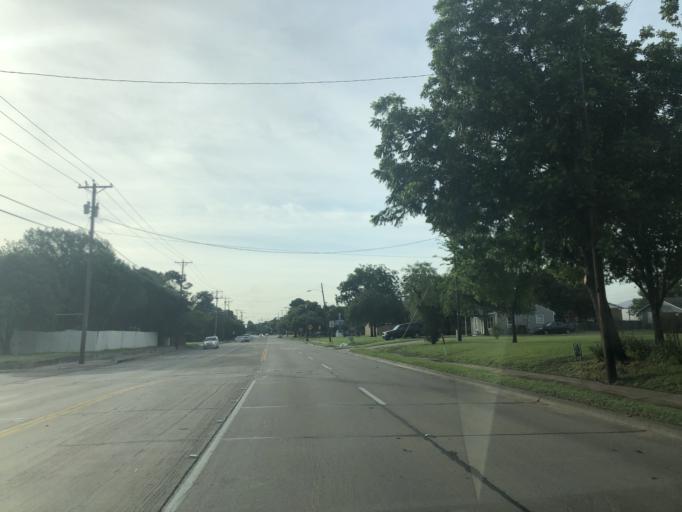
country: US
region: Texas
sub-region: Dallas County
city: Irving
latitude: 32.8030
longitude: -96.9889
